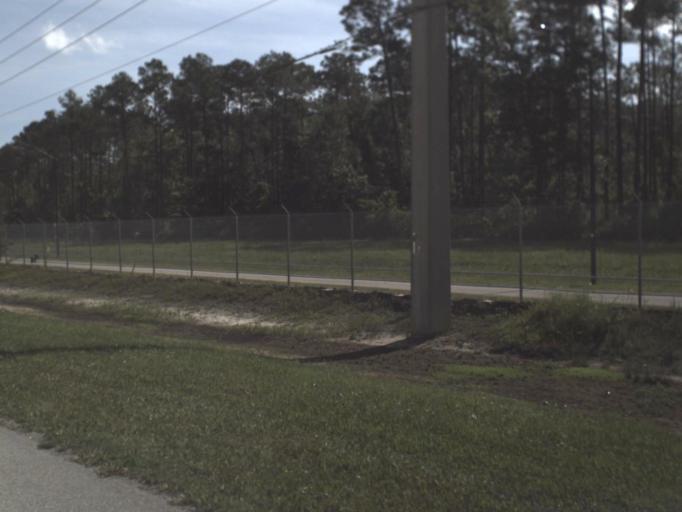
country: US
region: Florida
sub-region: Clay County
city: Orange Park
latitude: 30.2027
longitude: -81.7074
